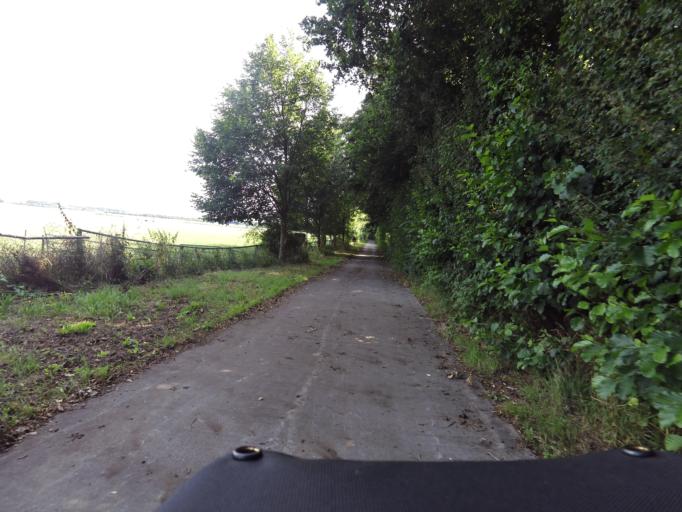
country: NL
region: South Holland
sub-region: Gemeente Goeree-Overflakkee
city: Ouddorp
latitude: 51.7986
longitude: 3.8704
